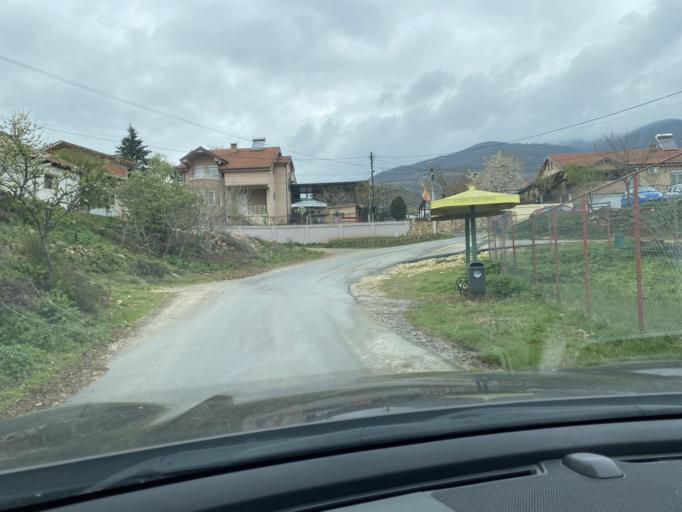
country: MK
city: Creshevo
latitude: 42.0515
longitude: 21.5187
